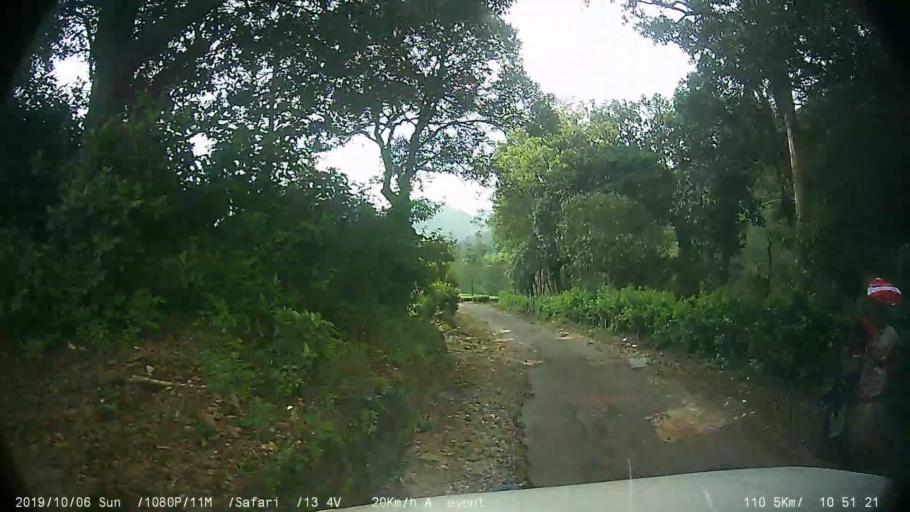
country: IN
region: Kerala
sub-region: Kottayam
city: Erattupetta
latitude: 9.6191
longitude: 76.9577
